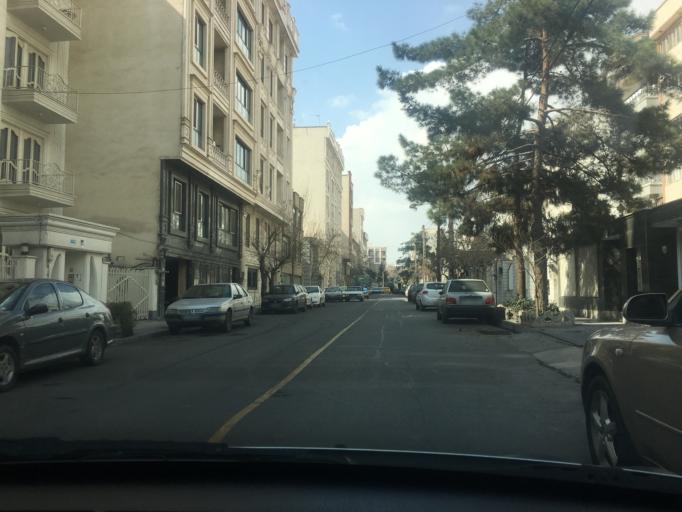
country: IR
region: Tehran
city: Tehran
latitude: 35.7206
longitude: 51.3198
